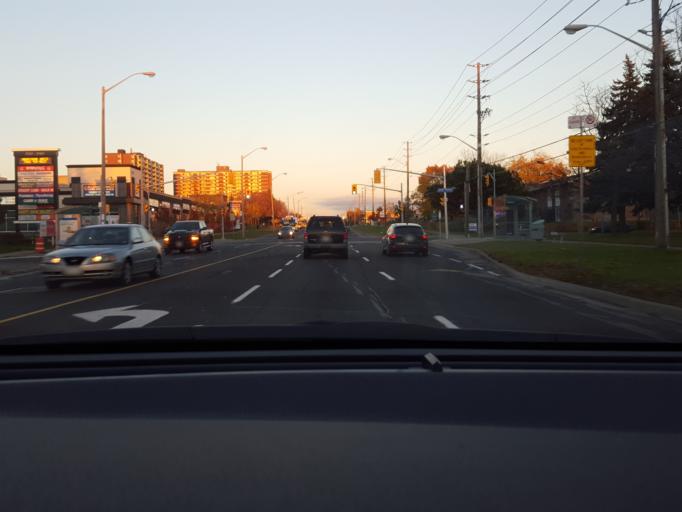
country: CA
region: Ontario
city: Scarborough
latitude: 43.7756
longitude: -79.2359
